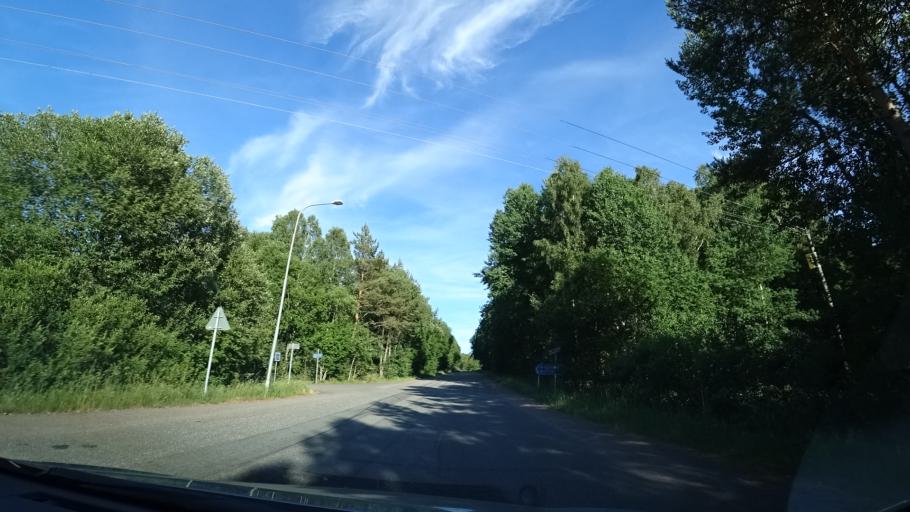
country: SE
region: Vaestra Goetaland
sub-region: Goteborg
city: Billdal
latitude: 57.5748
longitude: 11.9709
